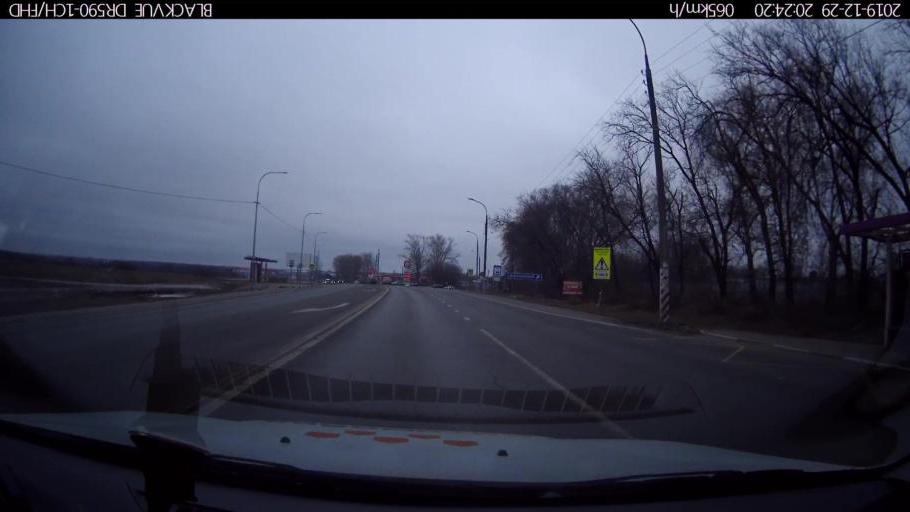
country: RU
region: Nizjnij Novgorod
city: Afonino
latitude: 56.2158
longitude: 44.1051
